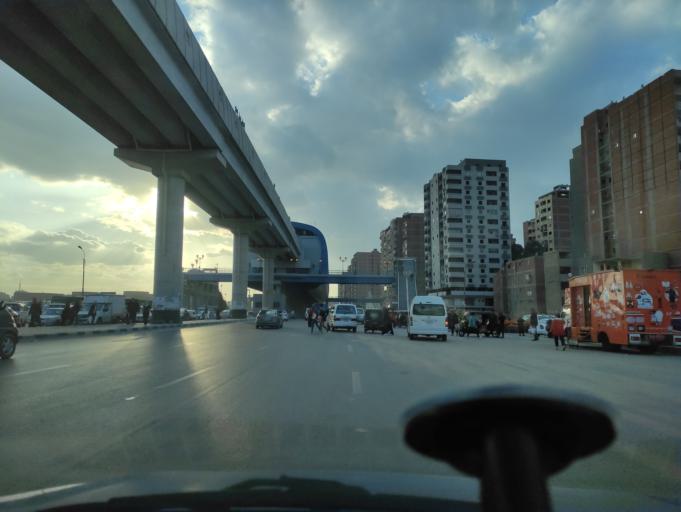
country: EG
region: Muhafazat al Qalyubiyah
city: Al Khankah
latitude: 30.1286
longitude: 31.3624
